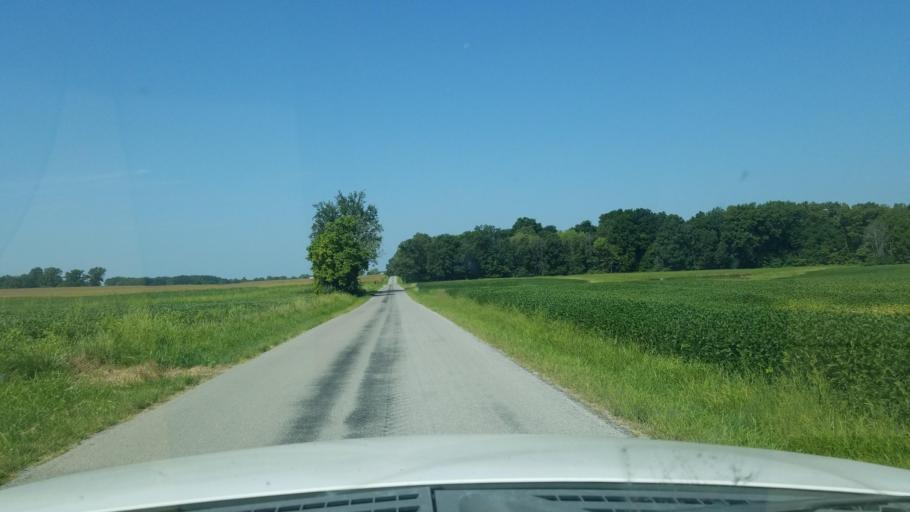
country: US
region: Illinois
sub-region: Saline County
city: Harrisburg
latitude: 37.8924
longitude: -88.6387
